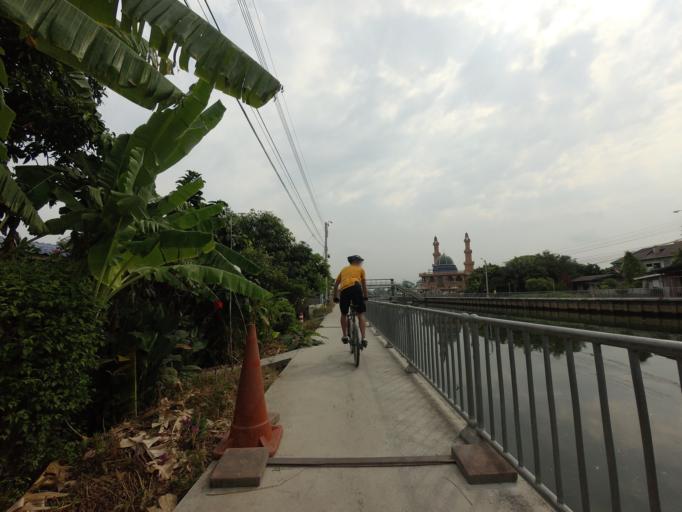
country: TH
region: Bangkok
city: Suan Luang
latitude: 13.7236
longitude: 100.6717
